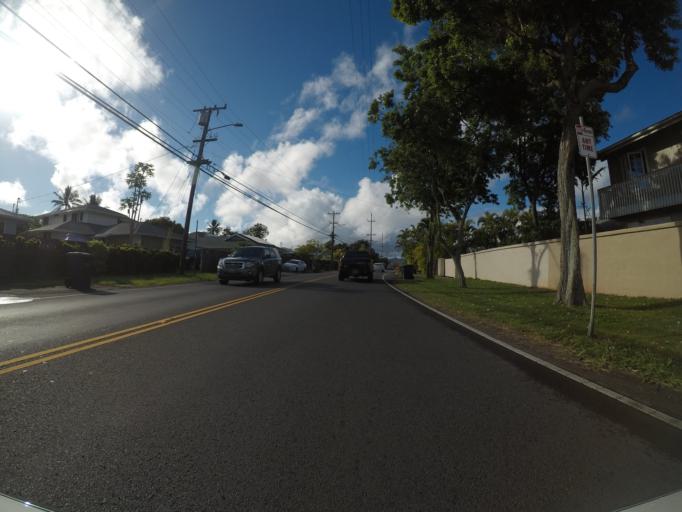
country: US
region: Hawaii
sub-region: Honolulu County
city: Kailua
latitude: 21.4077
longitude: -157.7523
